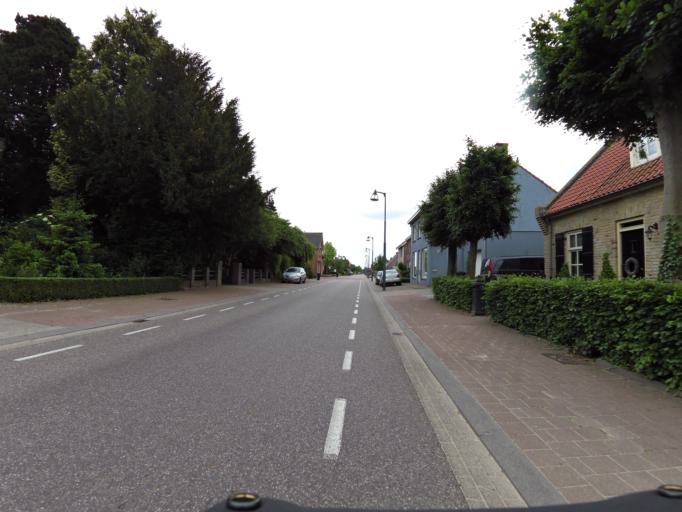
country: BE
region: Flanders
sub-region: Provincie Antwerpen
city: Baarle-Hertog
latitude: 51.4566
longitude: 4.8606
